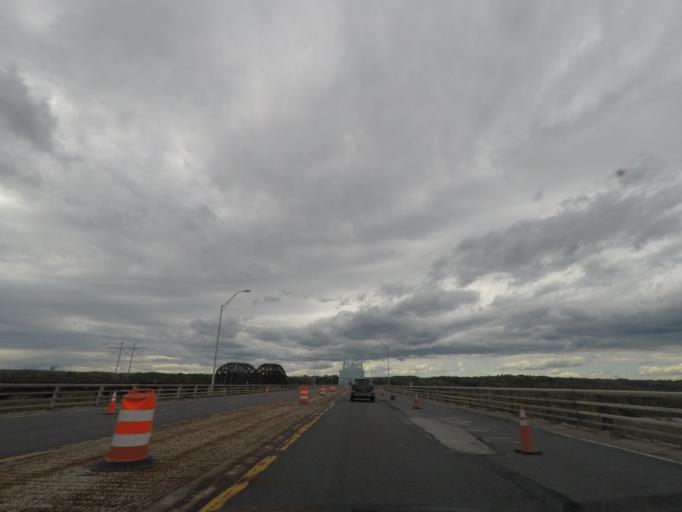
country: US
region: New York
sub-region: Rensselaer County
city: Castleton-on-Hudson
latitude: 42.5078
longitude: -73.7681
